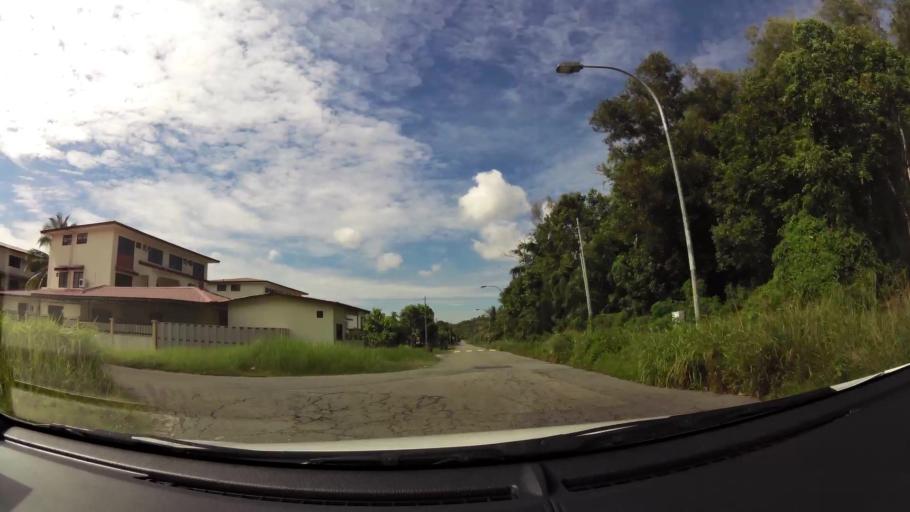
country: BN
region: Brunei and Muara
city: Bandar Seri Begawan
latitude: 4.9355
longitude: 114.9091
